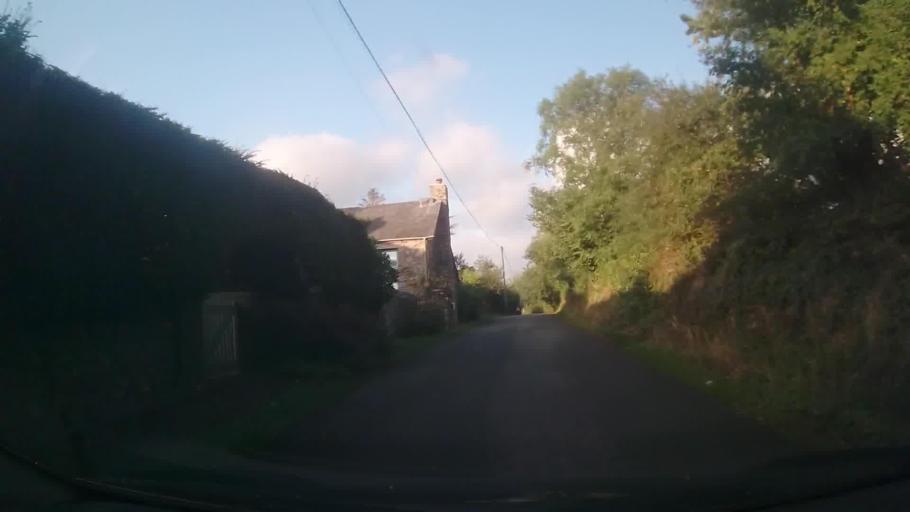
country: GB
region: Wales
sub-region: Pembrokeshire
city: Saundersfoot
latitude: 51.7518
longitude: -4.6525
